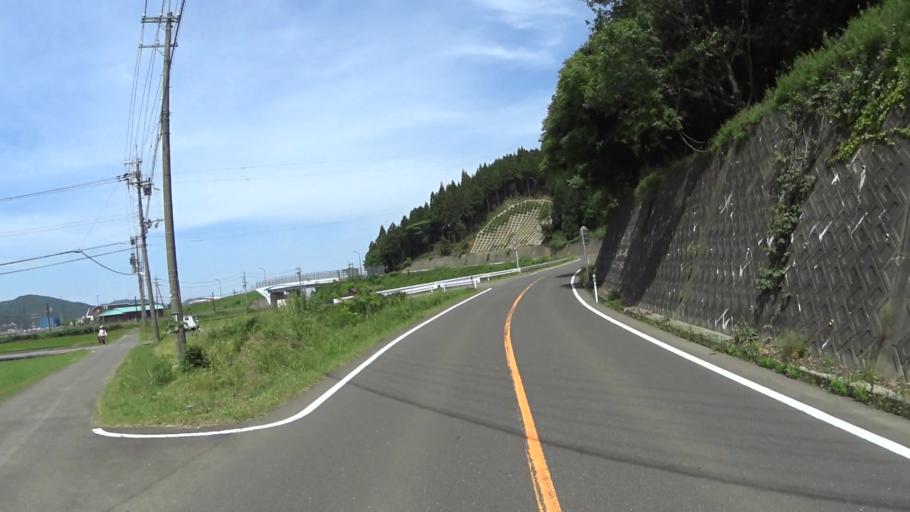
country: JP
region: Fukui
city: Obama
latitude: 35.4762
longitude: 135.6333
